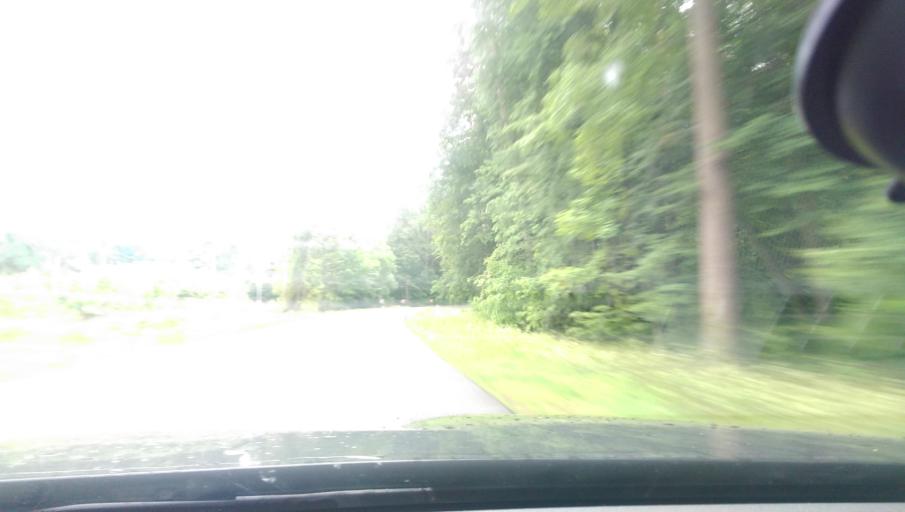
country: PL
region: Warmian-Masurian Voivodeship
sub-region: Powiat piski
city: Ruciane-Nida
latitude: 53.6999
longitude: 21.4703
